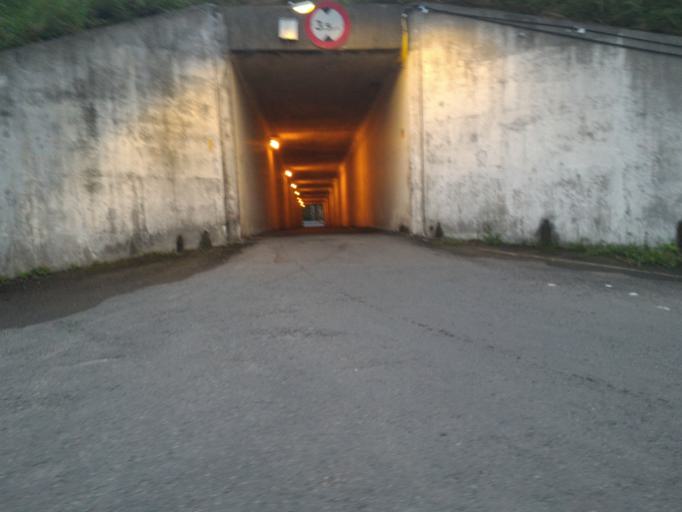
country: TW
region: Taiwan
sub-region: Taoyuan
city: Taoyuan
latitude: 24.9514
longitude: 121.4001
